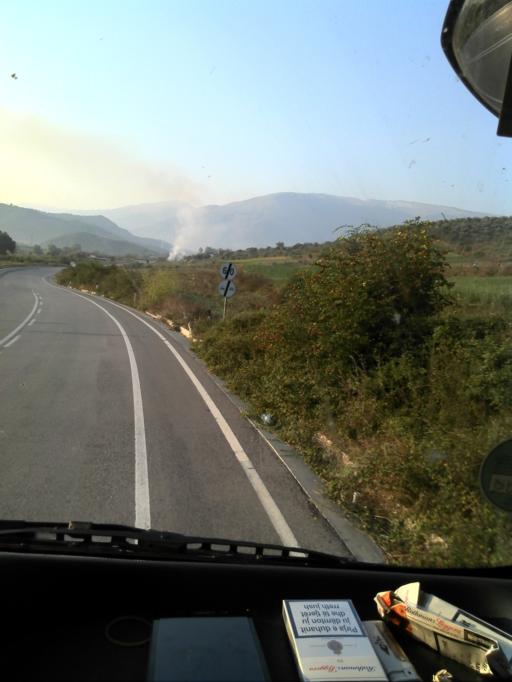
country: AL
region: Gjirokaster
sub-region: Rrethi i Tepelenes
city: Krahes
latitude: 40.4396
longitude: 19.8491
